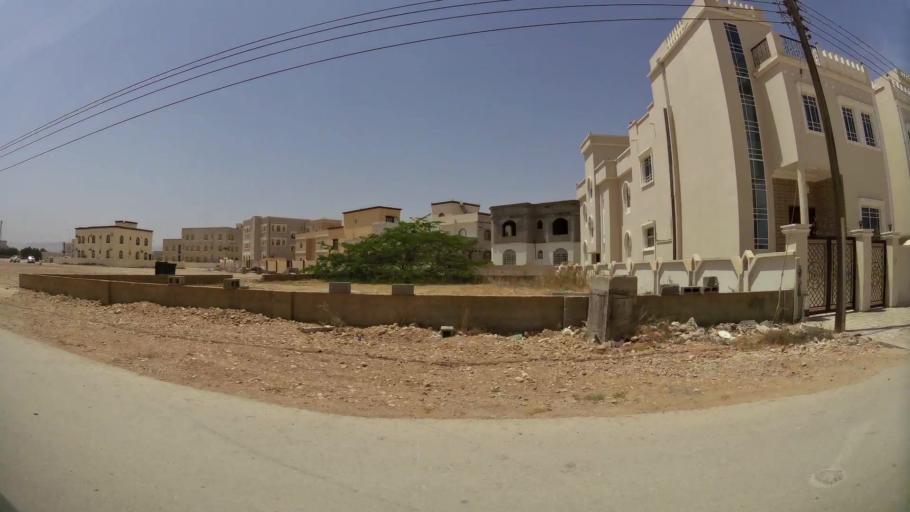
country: OM
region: Zufar
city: Salalah
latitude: 17.0604
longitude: 54.1582
